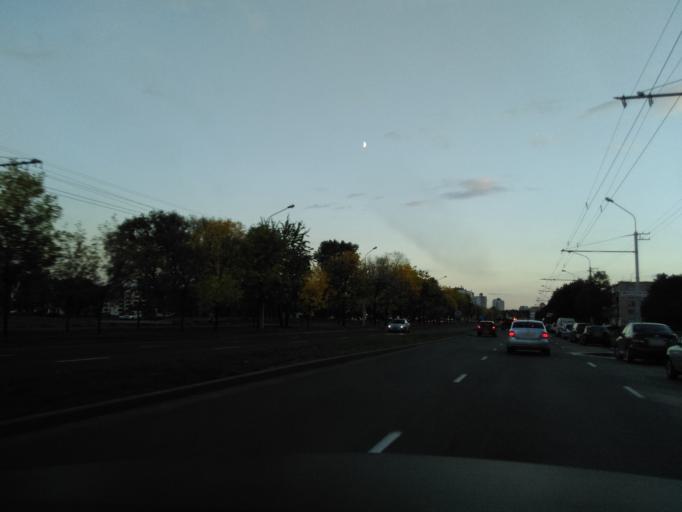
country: BY
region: Minsk
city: Minsk
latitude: 53.9233
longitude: 27.6382
